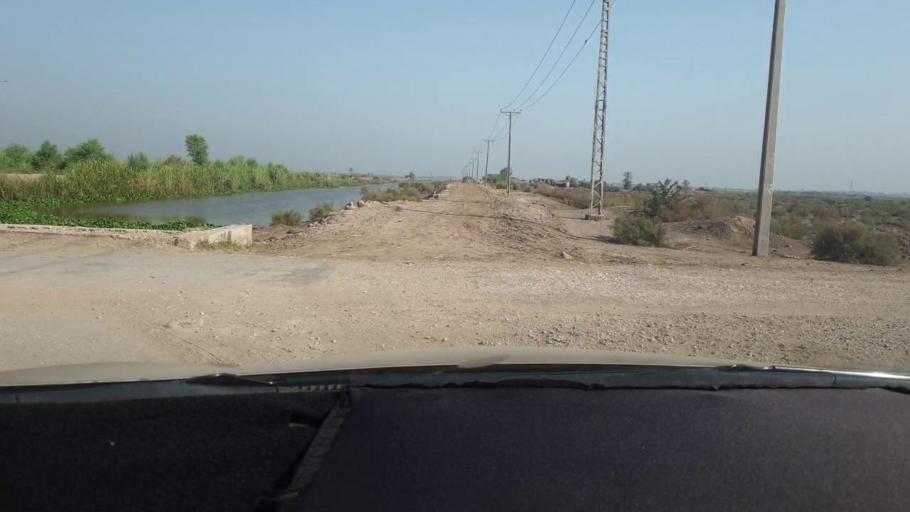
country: PK
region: Sindh
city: Miro Khan
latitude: 27.7642
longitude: 68.1335
